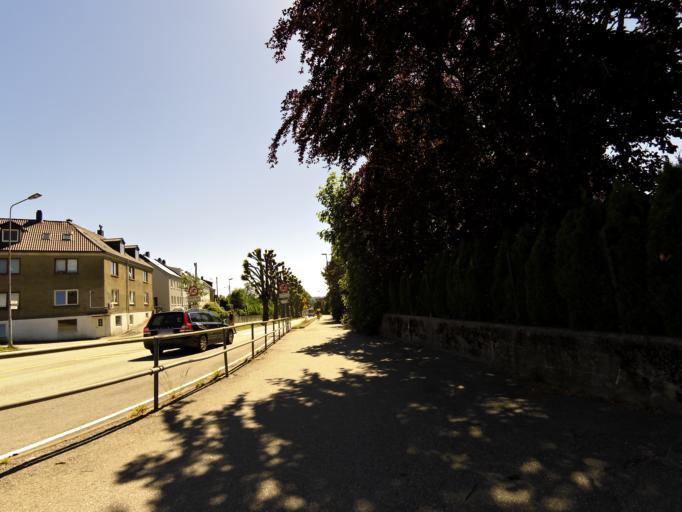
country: NO
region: Vest-Agder
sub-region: Kristiansand
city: Kristiansand
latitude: 58.1552
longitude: 8.0102
